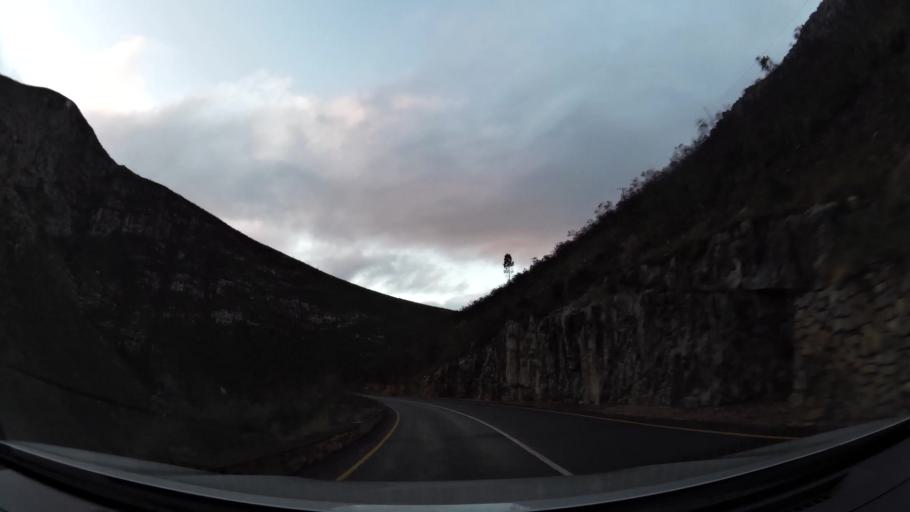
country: ZA
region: Western Cape
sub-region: Overberg District Municipality
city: Swellendam
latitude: -33.9622
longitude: 20.7036
